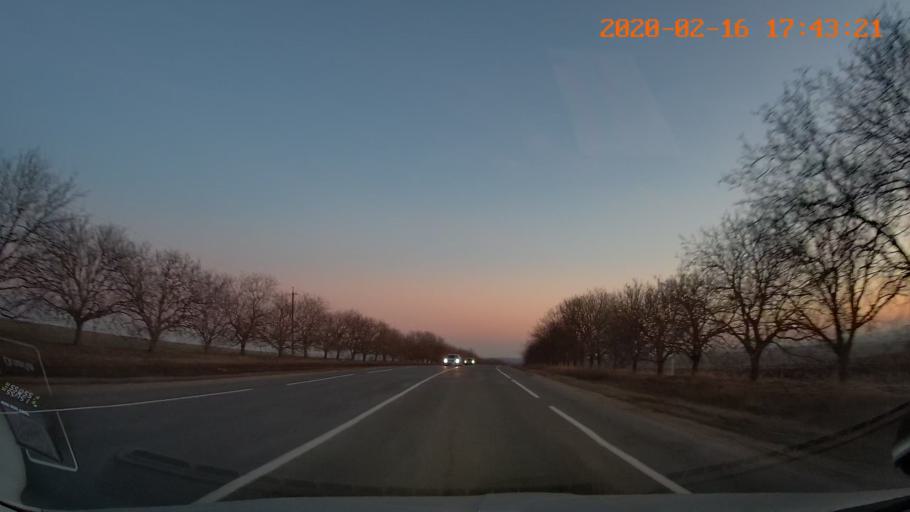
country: MD
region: Riscani
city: Riscani
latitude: 48.0141
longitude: 27.5652
